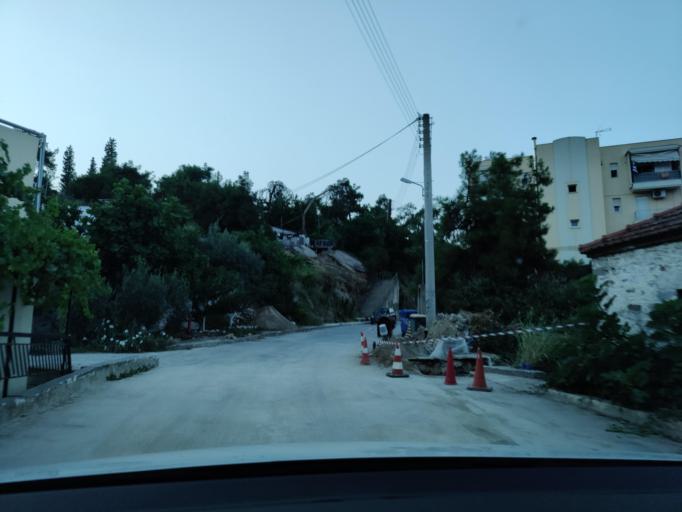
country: GR
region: East Macedonia and Thrace
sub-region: Nomos Kavalas
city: Kavala
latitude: 40.9280
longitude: 24.3889
